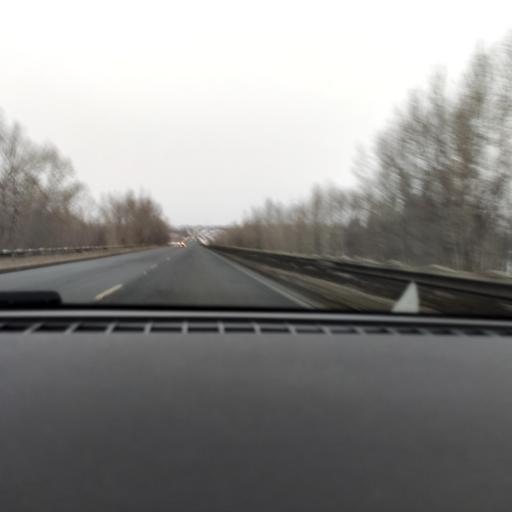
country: RU
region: Samara
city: Smyshlyayevka
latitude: 53.2259
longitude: 50.4951
